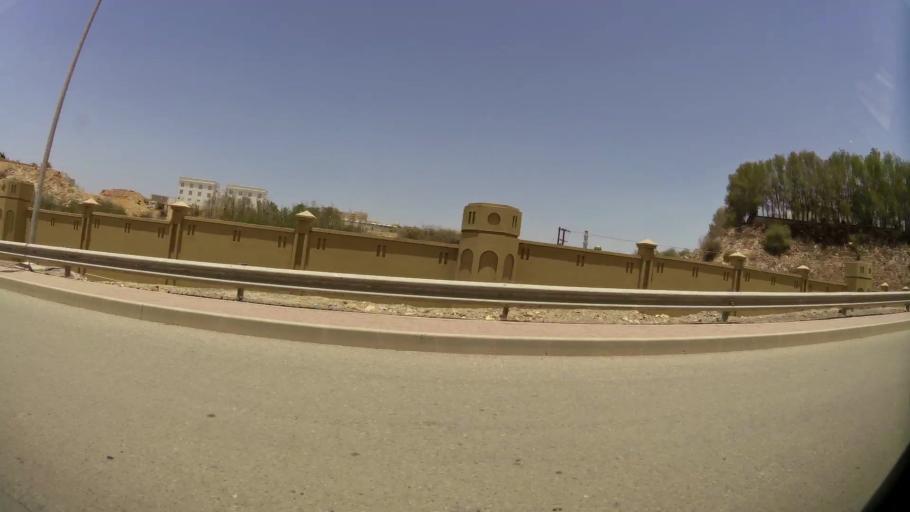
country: OM
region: Muhafazat Masqat
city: Bawshar
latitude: 23.6079
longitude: 58.4787
